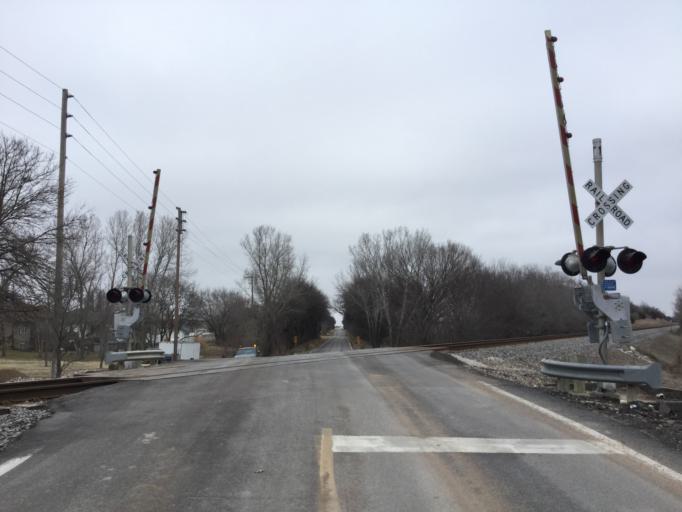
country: US
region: Kansas
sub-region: Sumner County
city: Mulvane
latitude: 37.4823
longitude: -97.2264
